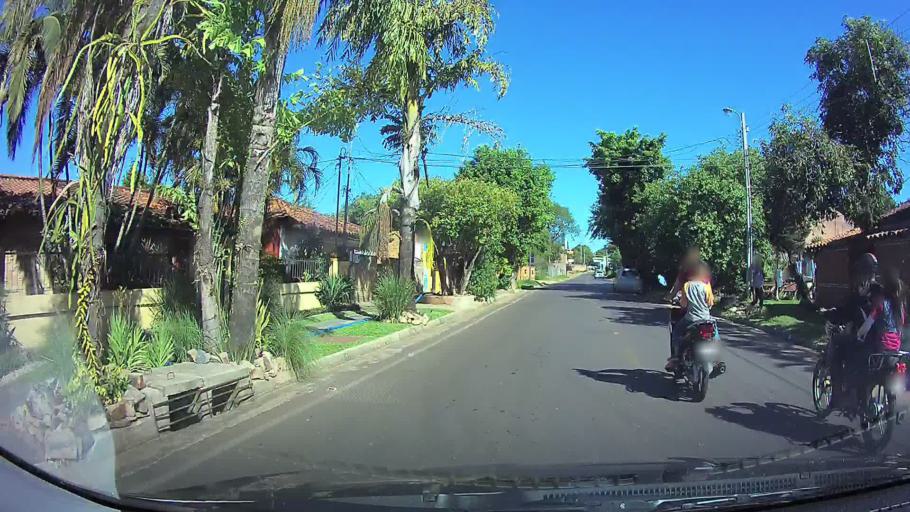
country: PY
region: Central
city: Fernando de la Mora
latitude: -25.2946
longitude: -57.5376
